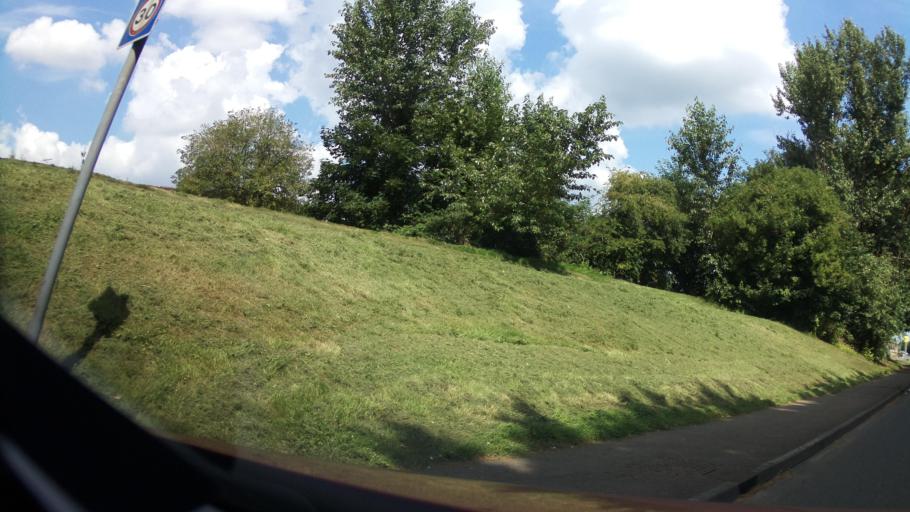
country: GB
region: England
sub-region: West Berkshire
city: Thatcham
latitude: 51.4015
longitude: -1.2787
